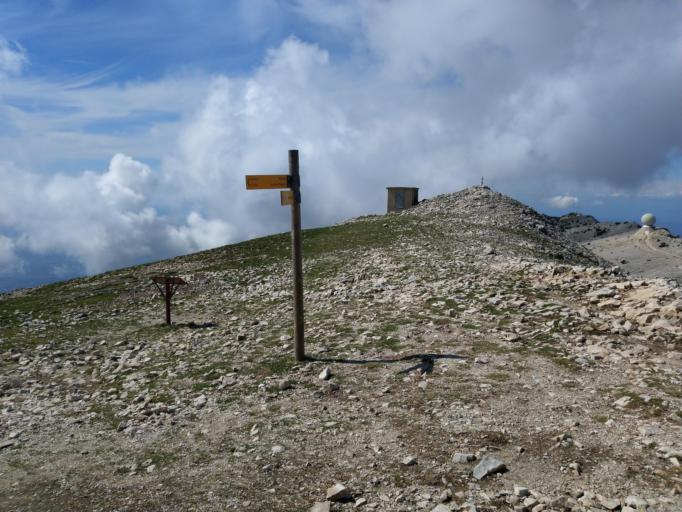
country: FR
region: Rhone-Alpes
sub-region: Departement de la Drome
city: Buis-les-Baronnies
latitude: 44.1732
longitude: 5.2755
